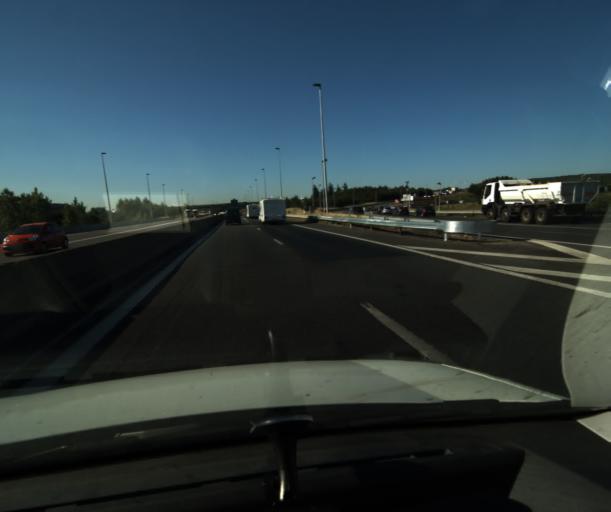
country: FR
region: Midi-Pyrenees
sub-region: Departement de la Haute-Garonne
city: Ramonville-Saint-Agne
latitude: 43.5606
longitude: 1.4938
